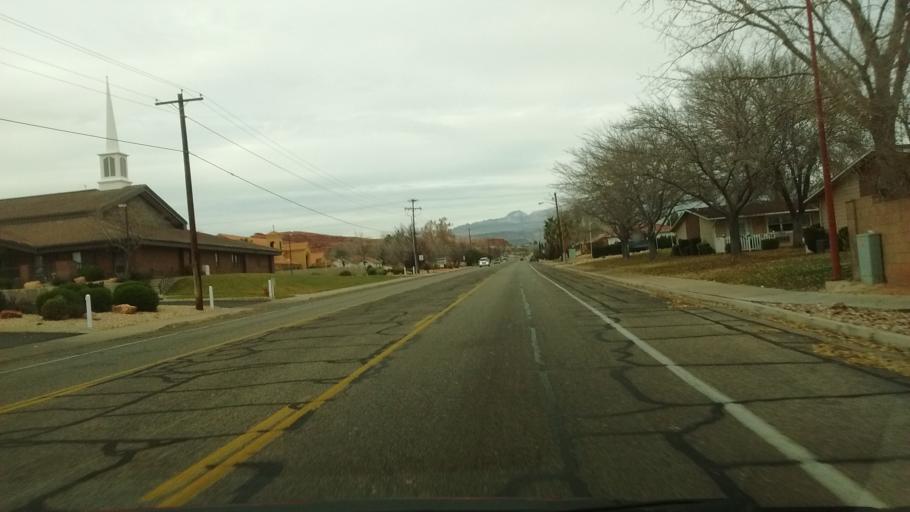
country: US
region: Utah
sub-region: Washington County
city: Washington
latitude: 37.1169
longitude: -113.5317
